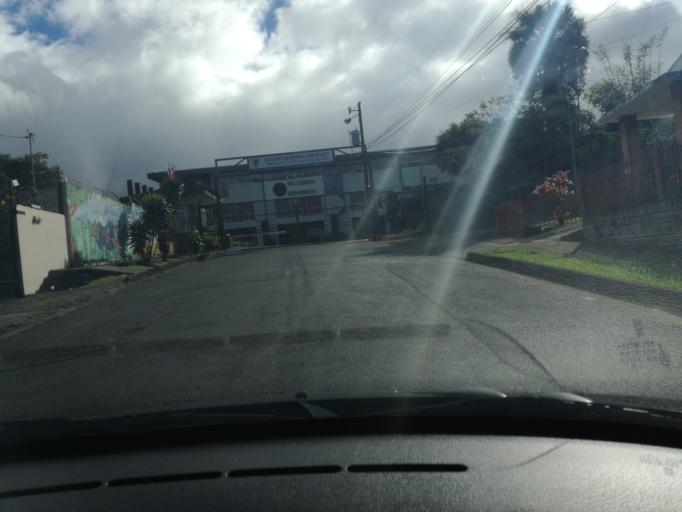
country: CR
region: San Jose
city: San Pedro
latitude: 9.9254
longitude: -84.0525
